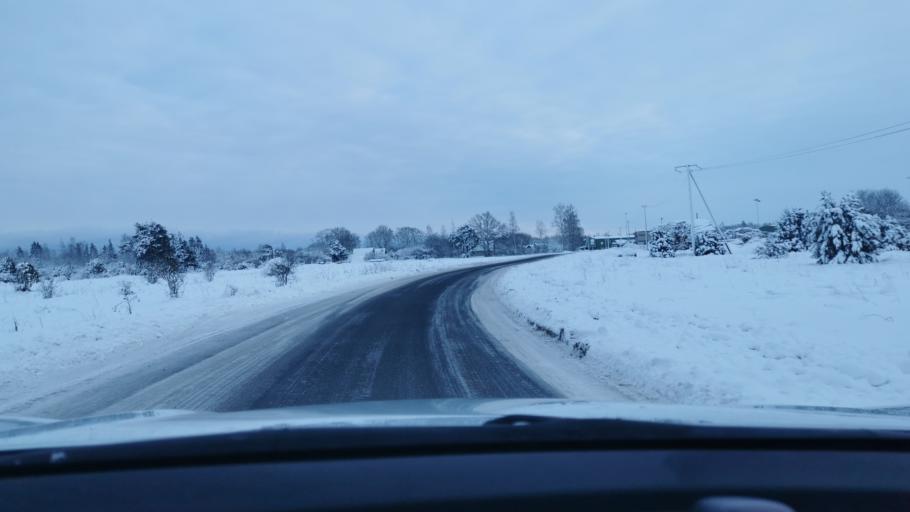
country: EE
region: Laeaene-Virumaa
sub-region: Viru-Nigula vald
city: Kunda
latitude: 59.4816
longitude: 26.4960
